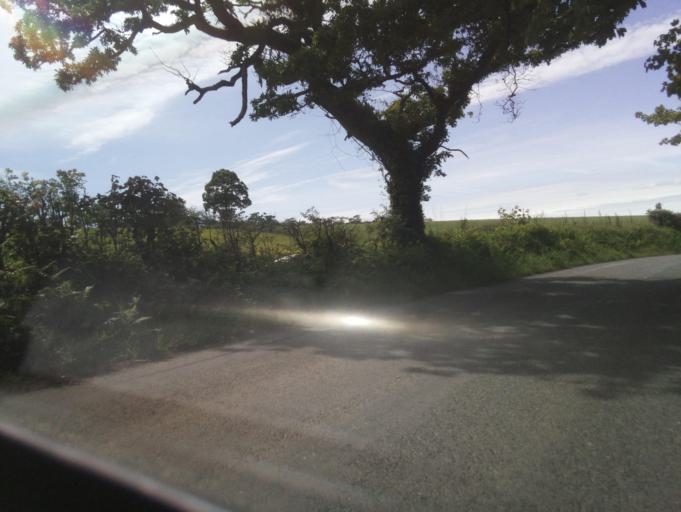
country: GB
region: England
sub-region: Devon
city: Kingsbridge
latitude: 50.3621
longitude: -3.7682
